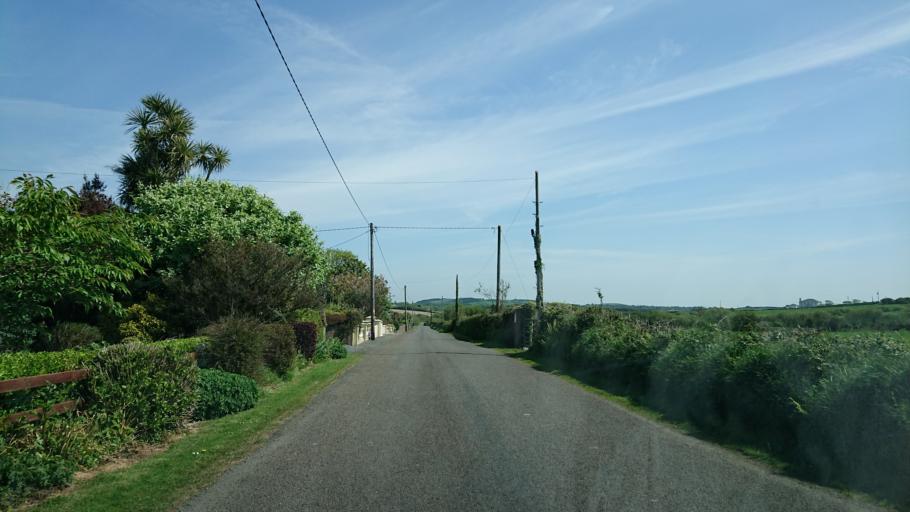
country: IE
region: Munster
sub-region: Waterford
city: Tra Mhor
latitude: 52.1559
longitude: -7.0698
